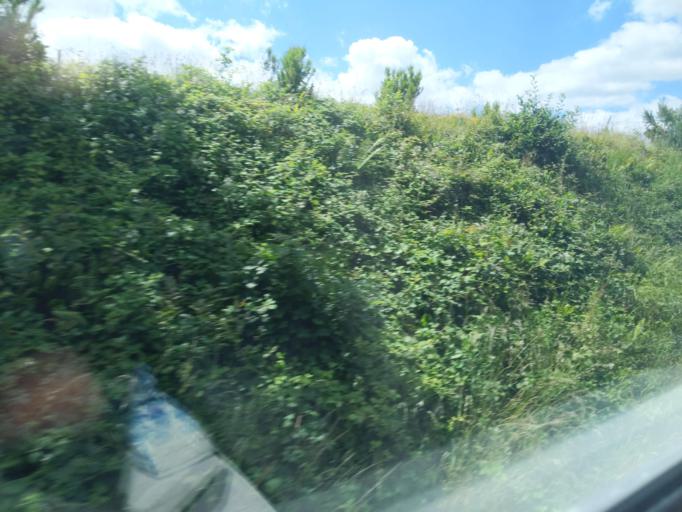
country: GB
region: England
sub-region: Cornwall
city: Liskeard
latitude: 50.4212
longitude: -4.3888
